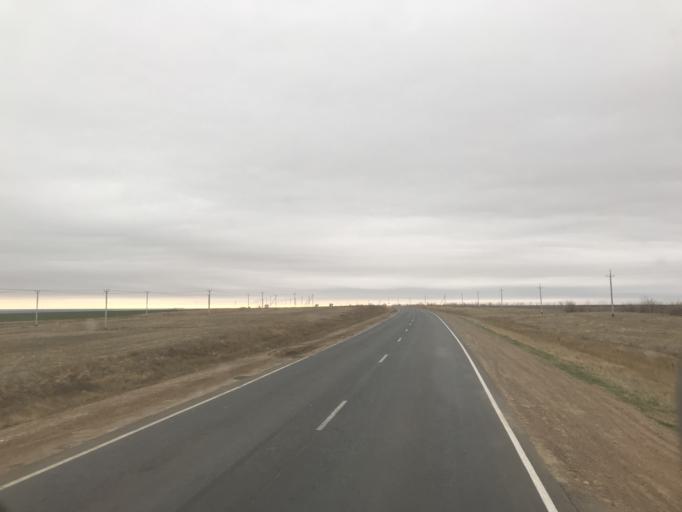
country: KZ
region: Batys Qazaqstan
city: Peremetnoe
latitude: 51.6462
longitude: 51.0127
